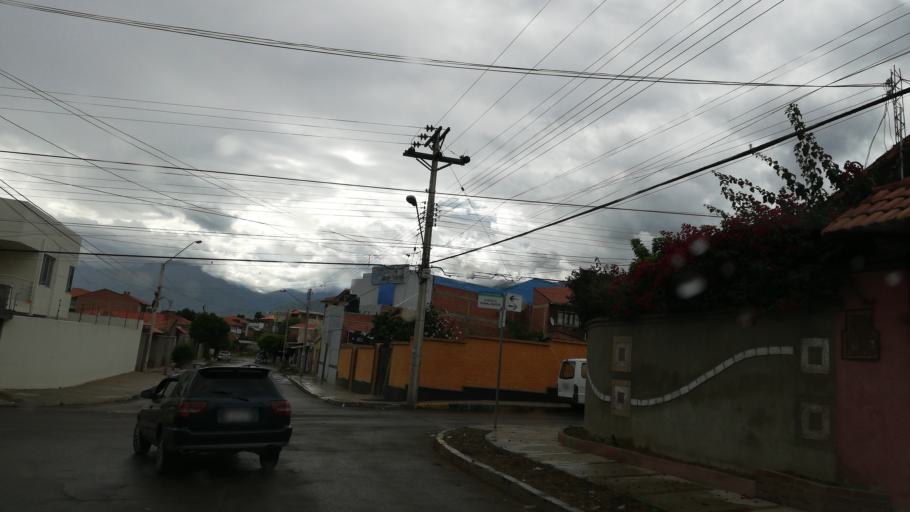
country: BO
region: Cochabamba
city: Cochabamba
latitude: -17.3483
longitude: -66.1788
